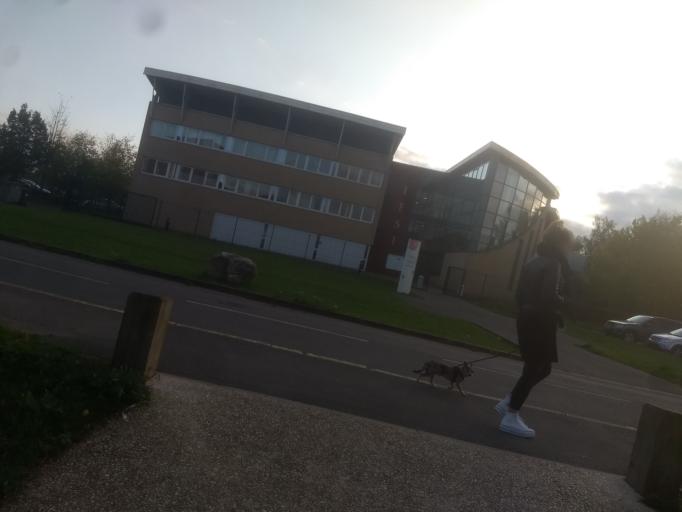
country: FR
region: Nord-Pas-de-Calais
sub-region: Departement du Pas-de-Calais
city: Saint-Laurent-Blangy
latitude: 50.2823
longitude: 2.7979
